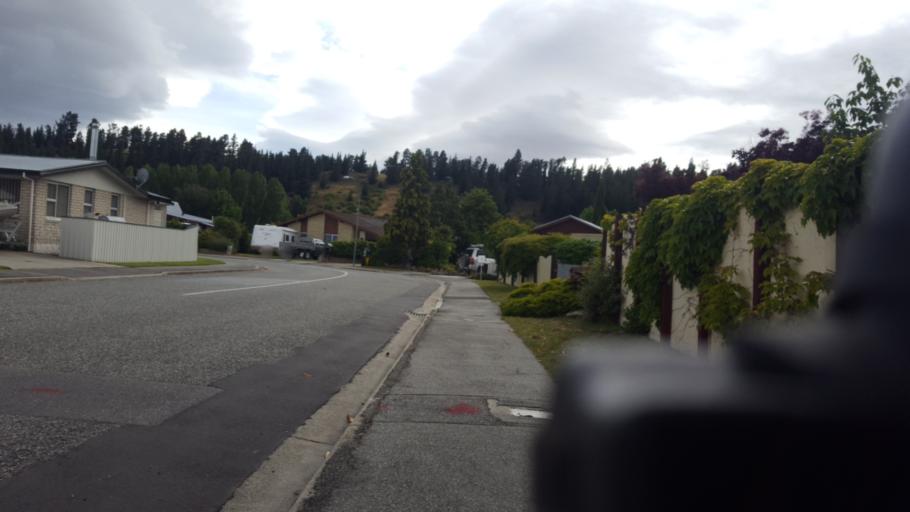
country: NZ
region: Otago
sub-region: Queenstown-Lakes District
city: Wanaka
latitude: -45.2429
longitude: 169.3930
